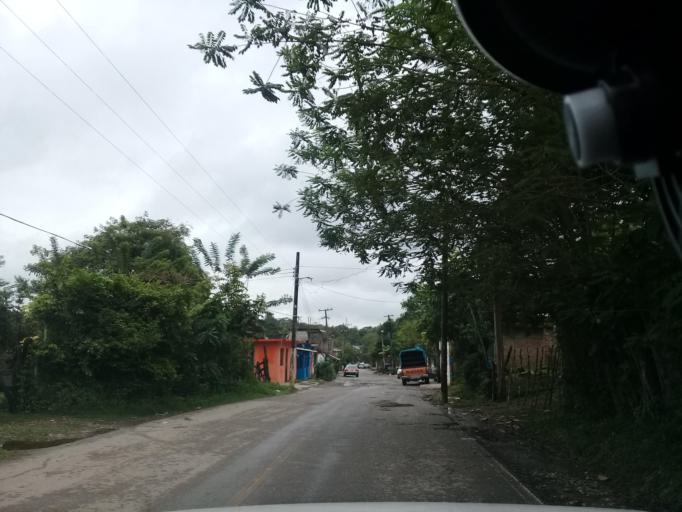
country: MX
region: Veracruz
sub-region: Chalma
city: San Pedro Coyutla
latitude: 21.2089
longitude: -98.4030
